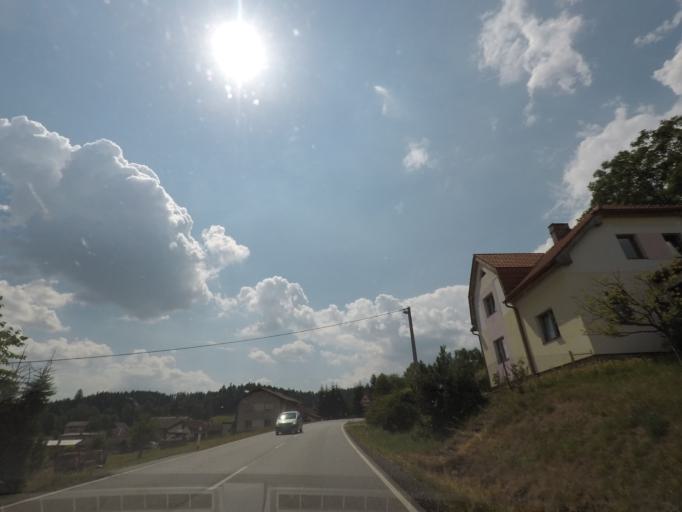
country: CZ
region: Liberecky
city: Studenec
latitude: 50.5270
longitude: 15.5841
